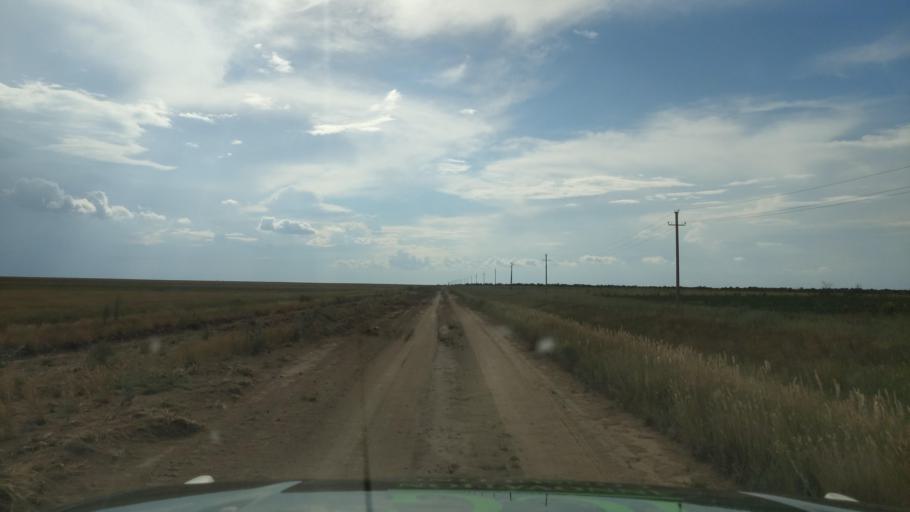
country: KZ
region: Pavlodar
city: Pavlodar
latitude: 52.5123
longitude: 77.5311
